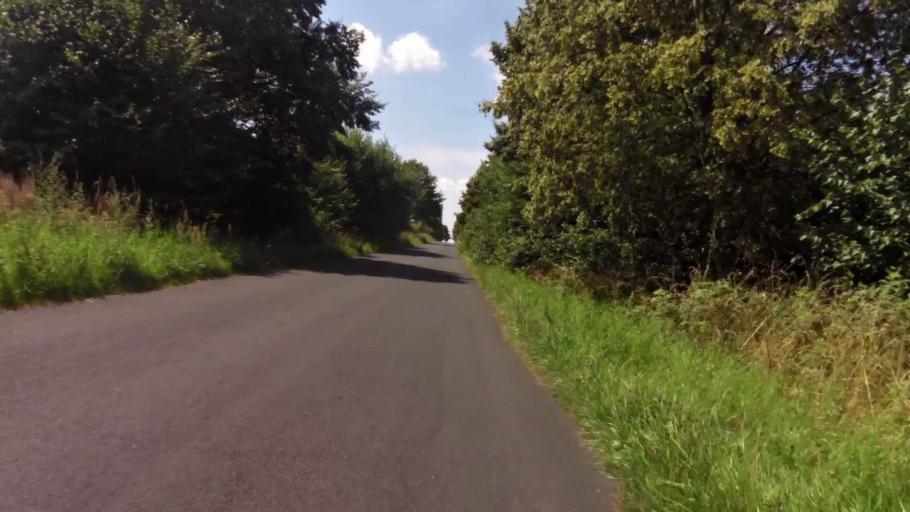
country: PL
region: West Pomeranian Voivodeship
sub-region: Powiat stargardzki
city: Dobrzany
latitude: 53.4267
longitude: 15.4199
